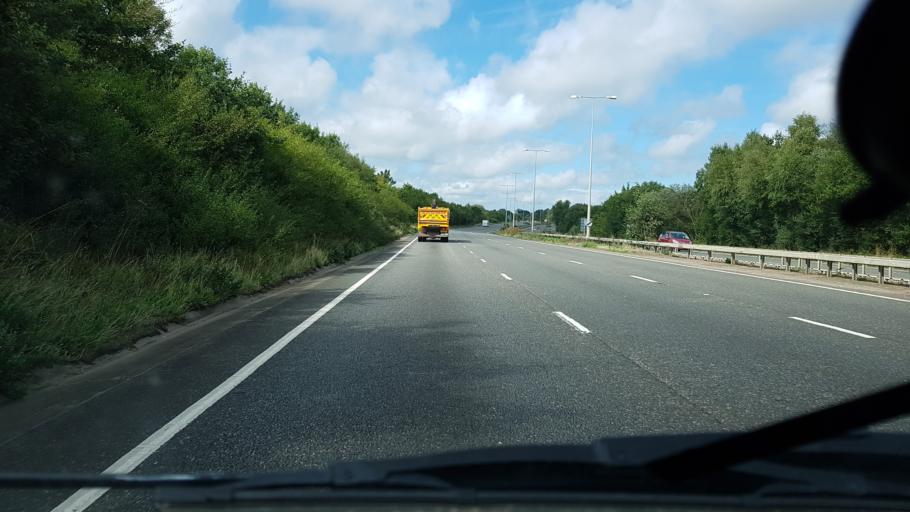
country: GB
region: England
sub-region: West Sussex
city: Broadfield
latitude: 51.0657
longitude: -0.2046
